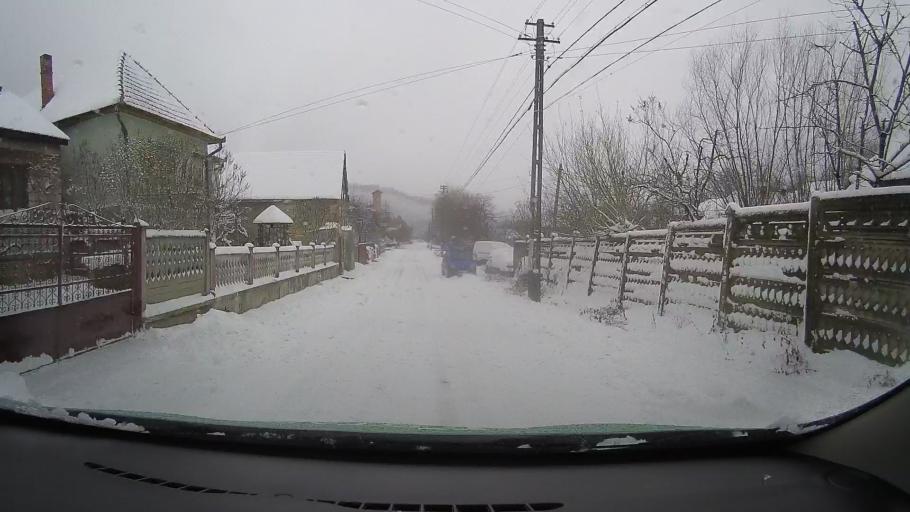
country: RO
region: Hunedoara
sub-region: Comuna Carjiti
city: Carjiti
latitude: 45.8442
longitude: 22.8272
